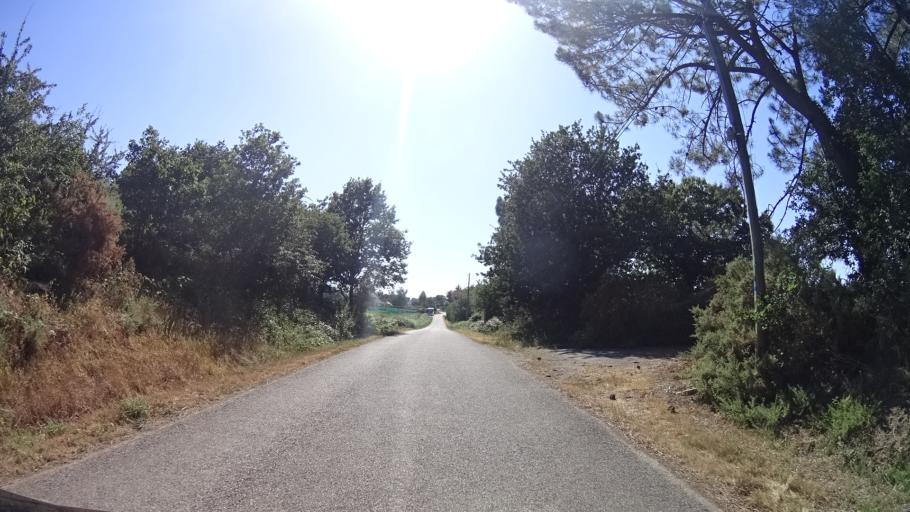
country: FR
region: Brittany
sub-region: Departement du Morbihan
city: Beganne
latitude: 47.5725
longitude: -2.2539
